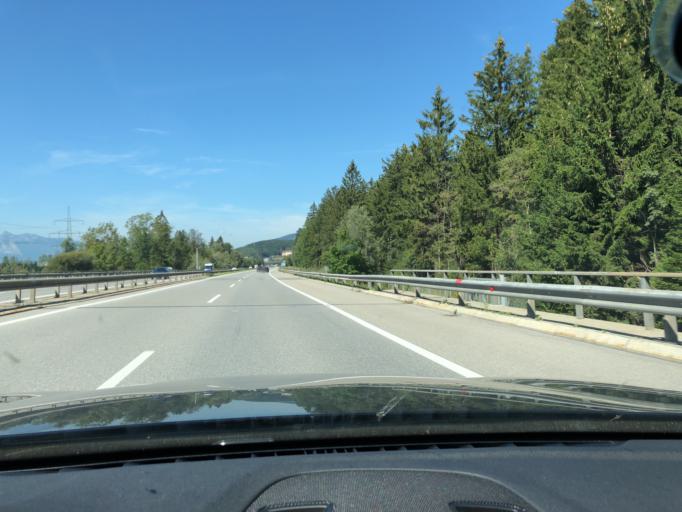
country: AT
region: Vorarlberg
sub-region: Politischer Bezirk Bludenz
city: Bludesch
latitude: 47.1824
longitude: 9.7263
